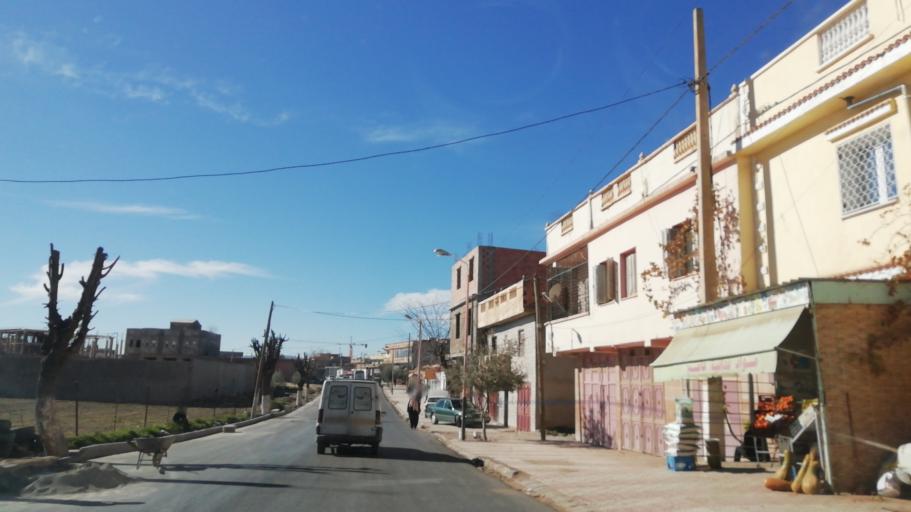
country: DZ
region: Tlemcen
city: Sebdou
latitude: 34.6535
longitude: -1.3164
